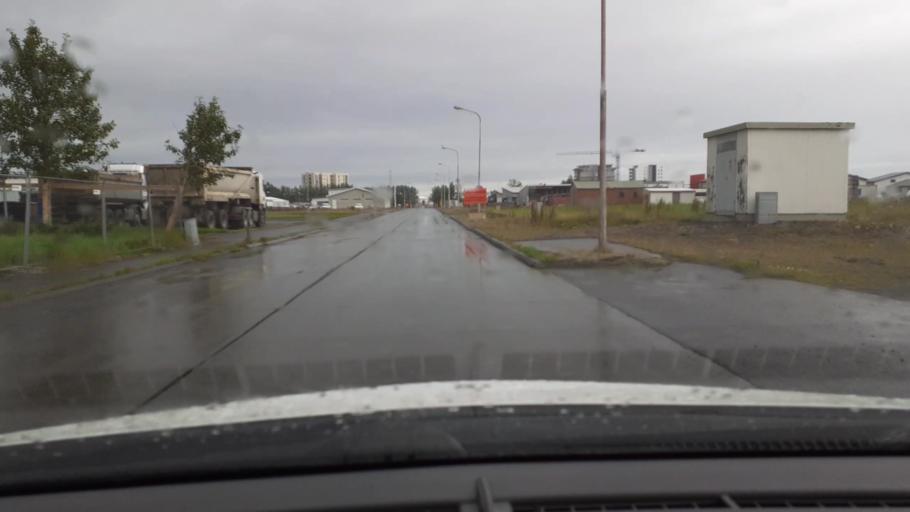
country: IS
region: West
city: Akranes
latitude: 64.3249
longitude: -22.0617
